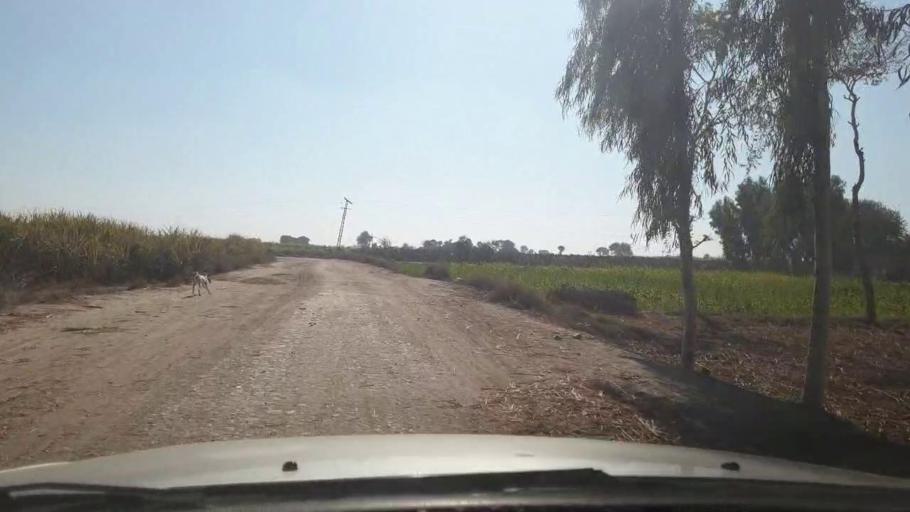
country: PK
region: Sindh
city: Ghotki
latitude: 28.0263
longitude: 69.2192
